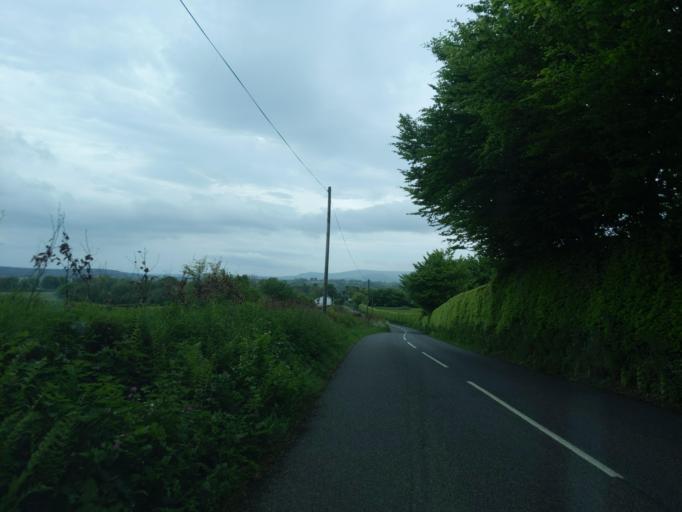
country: GB
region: England
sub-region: Devon
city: Tavistock
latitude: 50.6063
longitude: -4.1631
